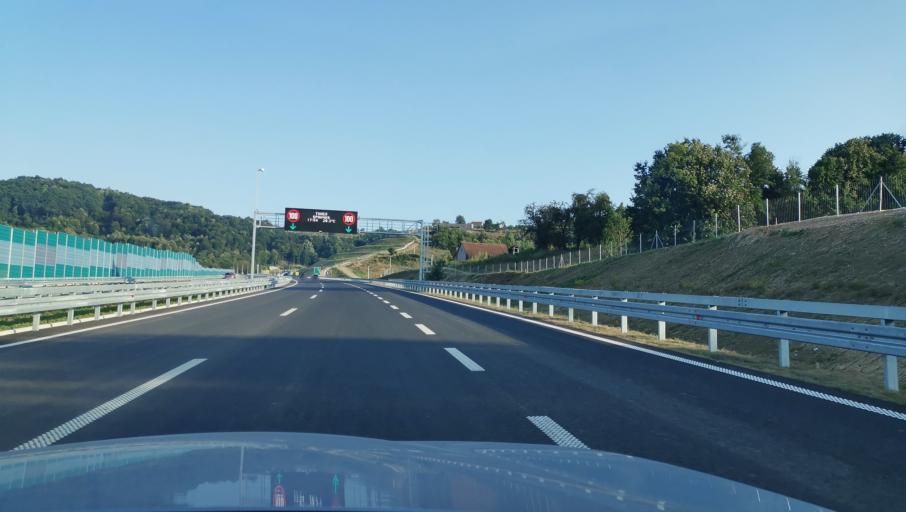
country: RS
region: Central Serbia
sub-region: Kolubarski Okrug
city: Ljig
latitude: 44.2181
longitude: 20.2572
